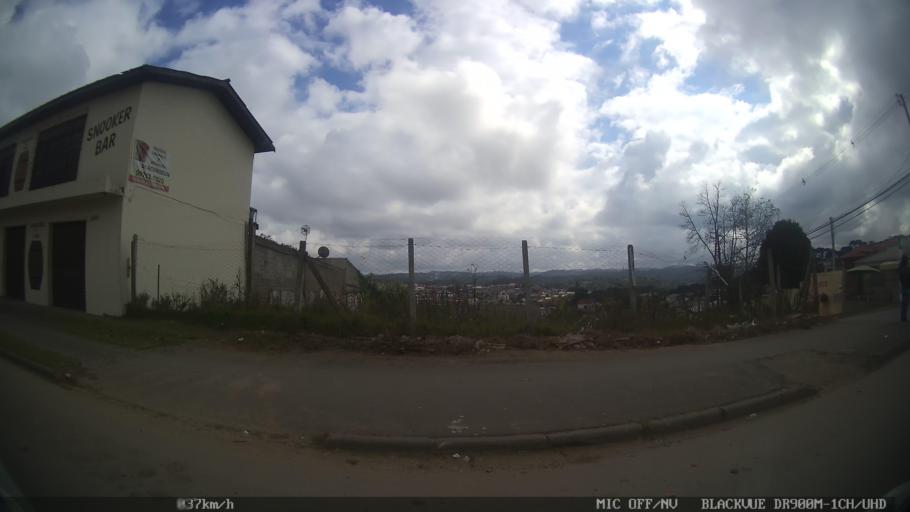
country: BR
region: Parana
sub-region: Colombo
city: Colombo
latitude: -25.3458
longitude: -49.2450
